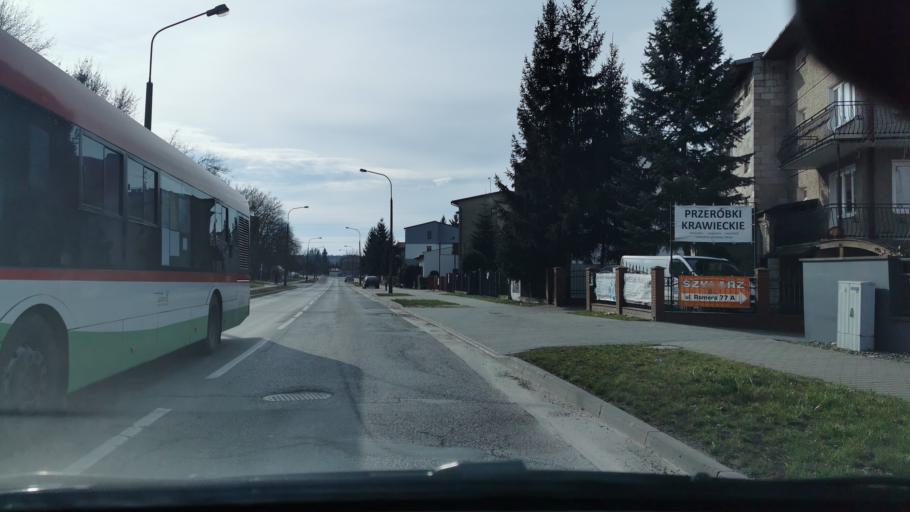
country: PL
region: Lublin Voivodeship
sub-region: Powiat lubelski
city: Lublin
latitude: 51.2075
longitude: 22.5416
